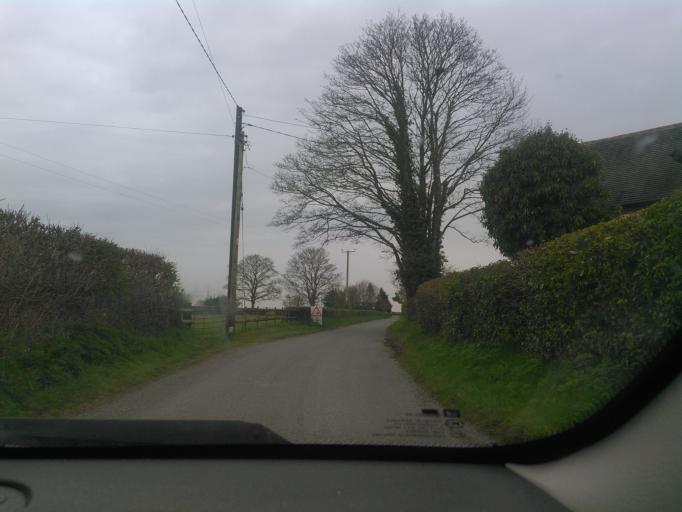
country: GB
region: England
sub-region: Shropshire
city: Stoke upon Tern
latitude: 52.7938
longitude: -2.5746
